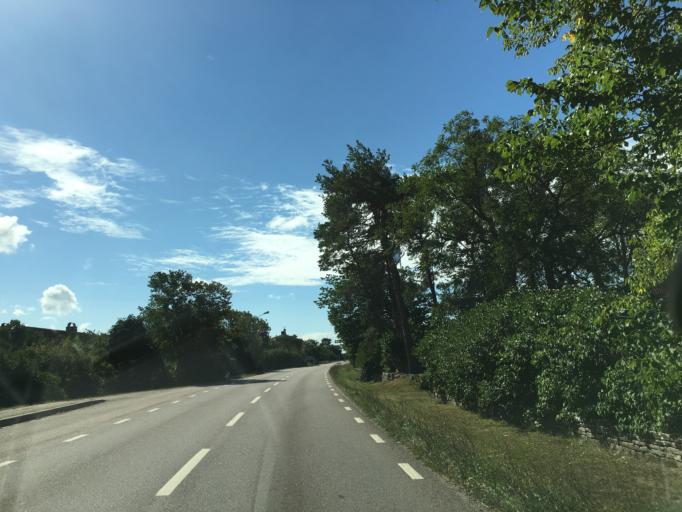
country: SE
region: Kalmar
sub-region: Morbylanga Kommun
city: Moerbylanga
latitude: 56.5398
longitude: 16.4456
